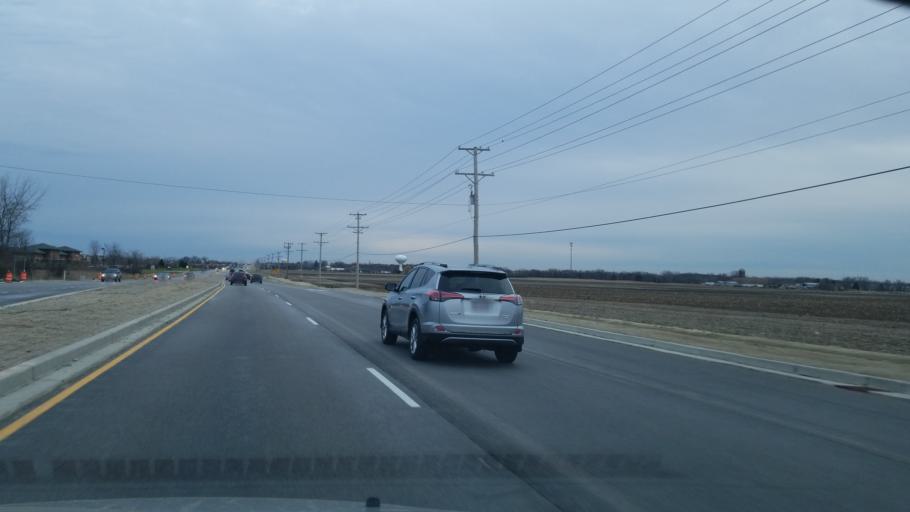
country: US
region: Illinois
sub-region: McHenry County
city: Lake in the Hills
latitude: 42.1389
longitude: -88.3359
